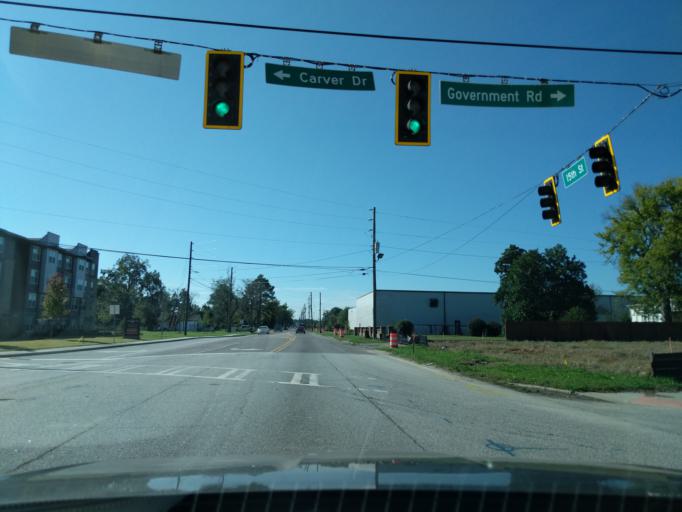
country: US
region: Georgia
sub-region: Richmond County
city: Augusta
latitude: 33.4616
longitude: -81.9959
